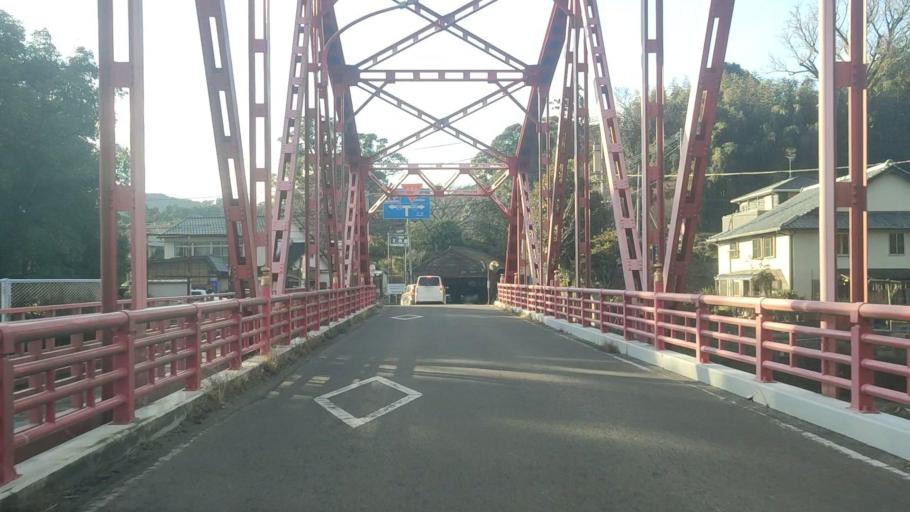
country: JP
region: Saga Prefecture
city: Saga-shi
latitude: 33.3270
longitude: 130.2688
